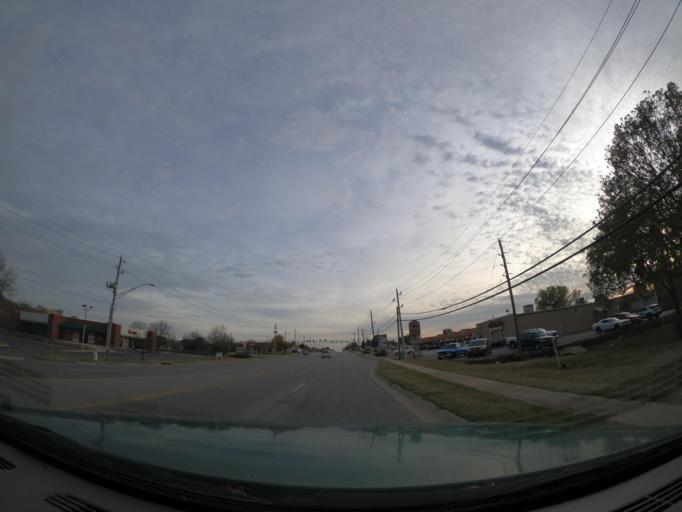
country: US
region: Oklahoma
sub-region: Tulsa County
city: Broken Arrow
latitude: 36.0480
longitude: -95.8155
